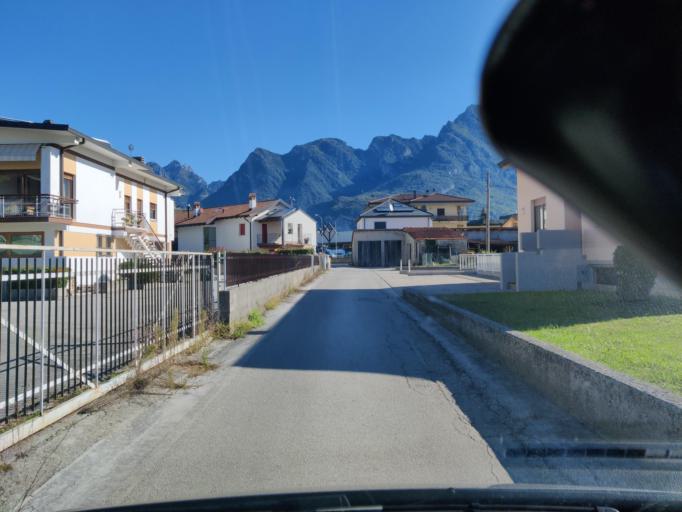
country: IT
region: Veneto
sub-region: Provincia di Belluno
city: Ponte nelle Alpi-Polpet
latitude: 46.1807
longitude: 12.2730
